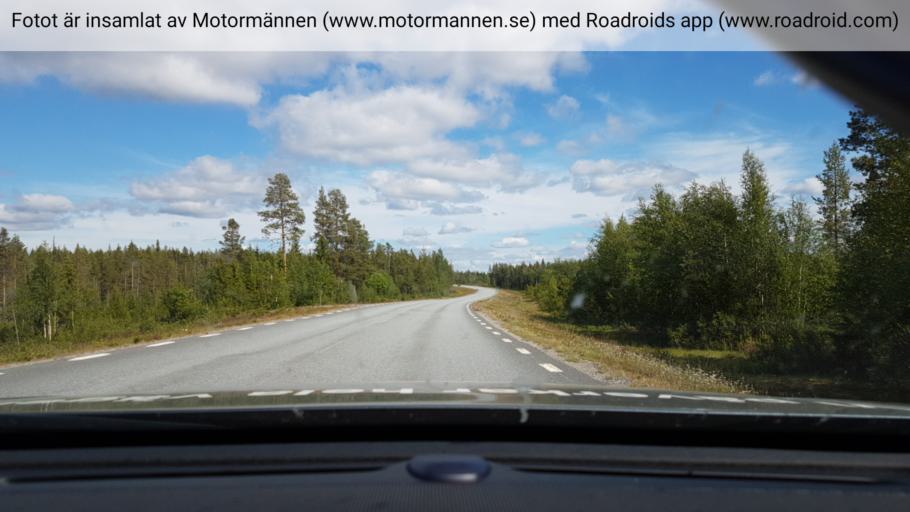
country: SE
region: Vaesterbotten
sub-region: Sorsele Kommun
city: Sorsele
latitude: 65.5577
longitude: 17.7506
